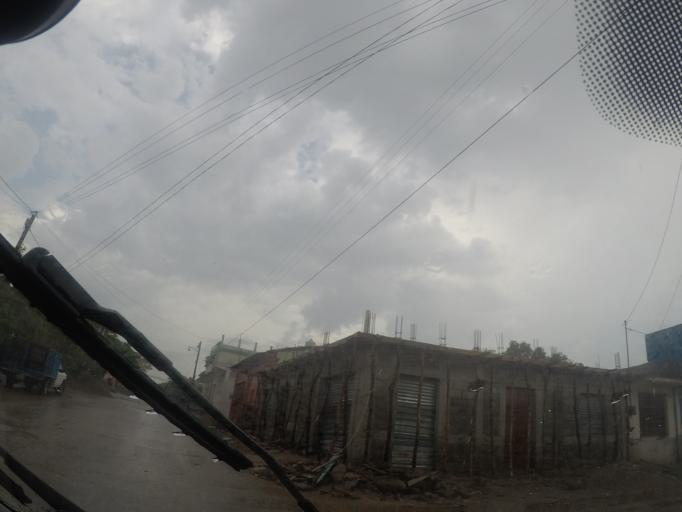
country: MX
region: Oaxaca
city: San Pedro Tapanatepec
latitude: 16.3677
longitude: -94.1929
